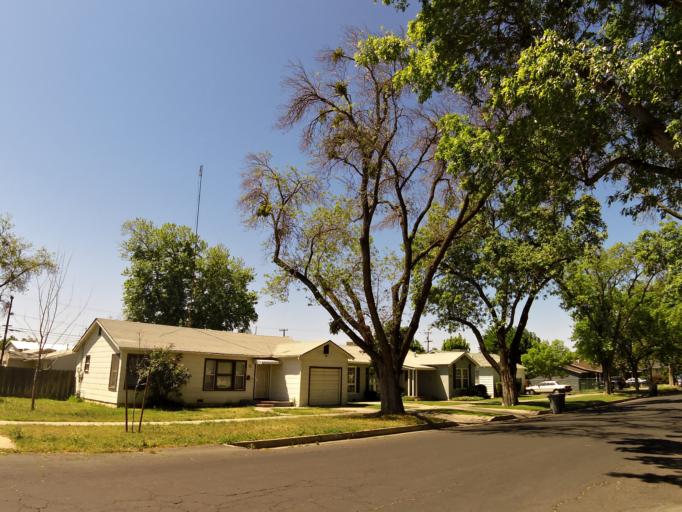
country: US
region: California
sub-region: Merced County
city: Merced
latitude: 37.3106
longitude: -120.4819
